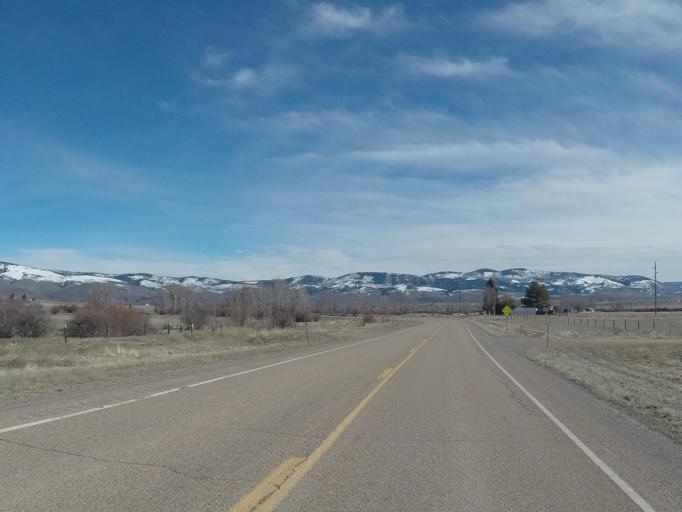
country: US
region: Montana
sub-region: Granite County
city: Philipsburg
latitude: 46.6093
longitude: -113.1821
